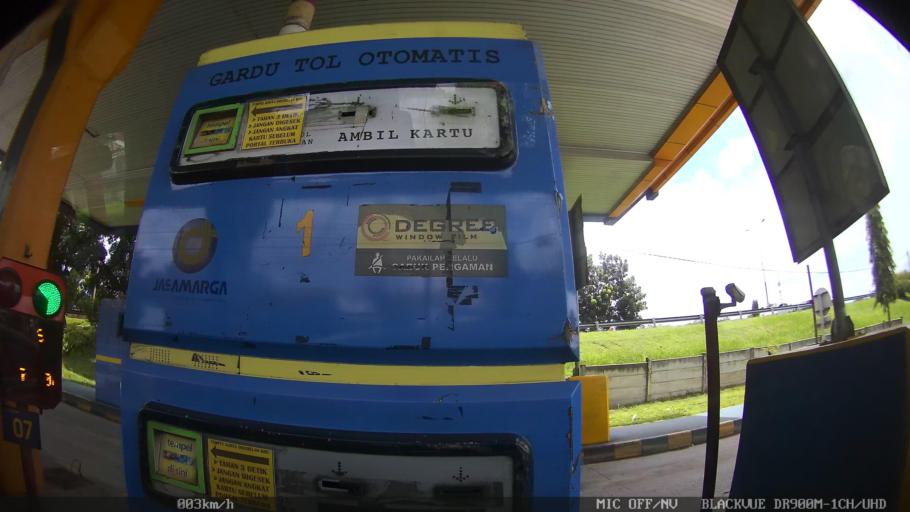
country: ID
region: North Sumatra
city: Medan
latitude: 3.5991
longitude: 98.7236
